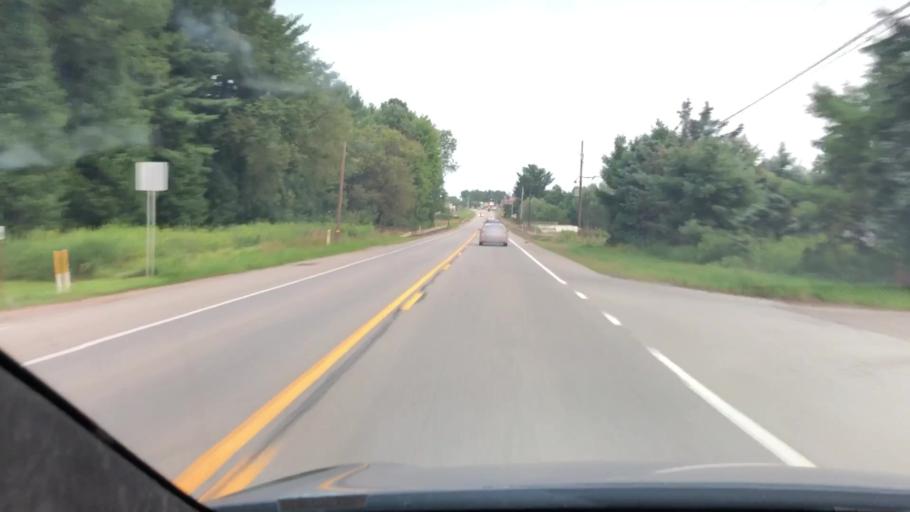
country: US
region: Pennsylvania
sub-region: Butler County
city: Shanor-Northvue
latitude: 40.9262
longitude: -79.9508
